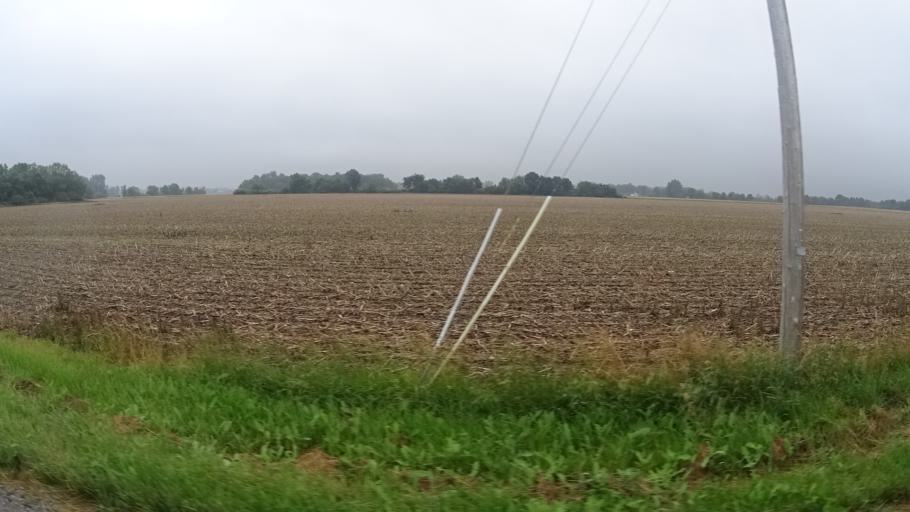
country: US
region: Ohio
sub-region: Huron County
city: Bellevue
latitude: 41.3623
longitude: -82.8142
